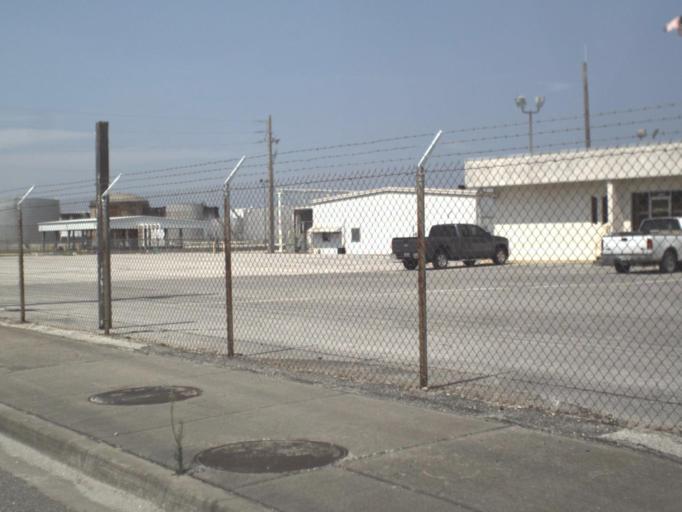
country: US
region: Florida
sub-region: Duval County
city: Jacksonville
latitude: 30.3583
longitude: -81.6267
